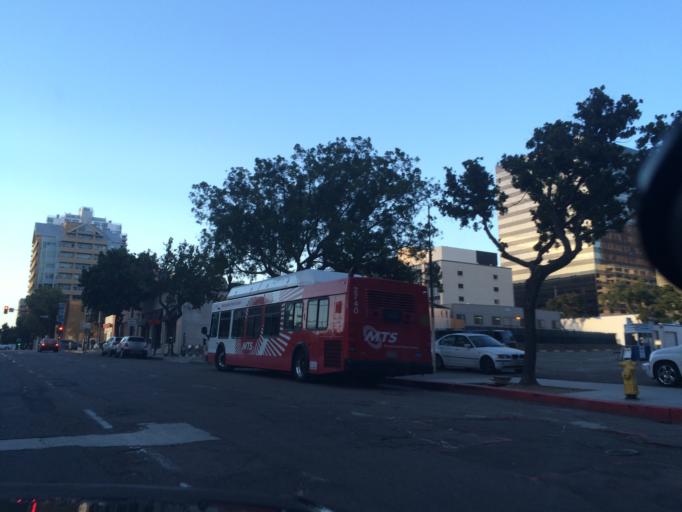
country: US
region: California
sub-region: San Diego County
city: San Diego
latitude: 32.7178
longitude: -117.1666
